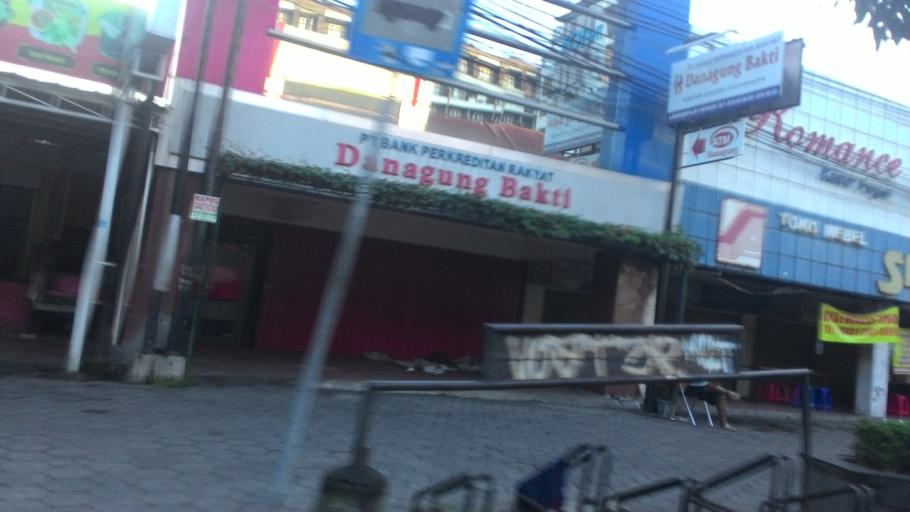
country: ID
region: Daerah Istimewa Yogyakarta
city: Yogyakarta
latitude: -7.7837
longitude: 110.3670
